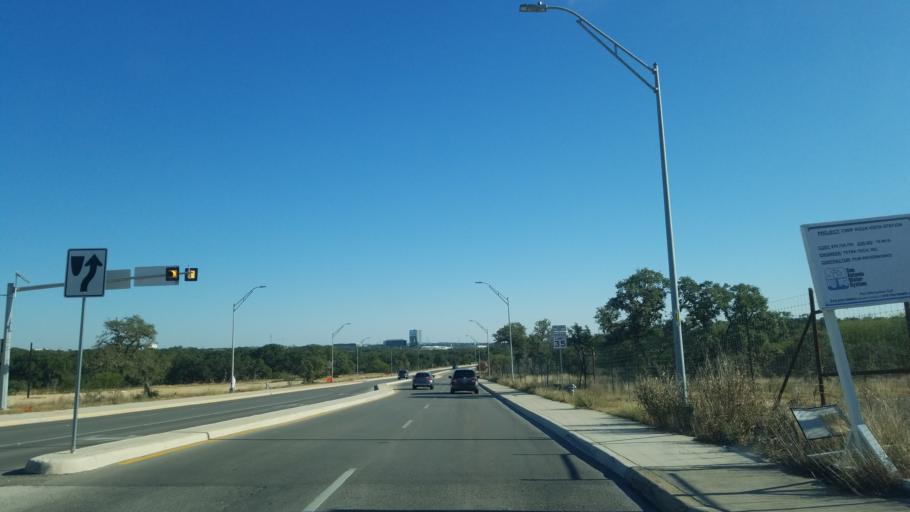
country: US
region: Texas
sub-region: Bexar County
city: Hollywood Park
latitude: 29.6301
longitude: -98.4802
